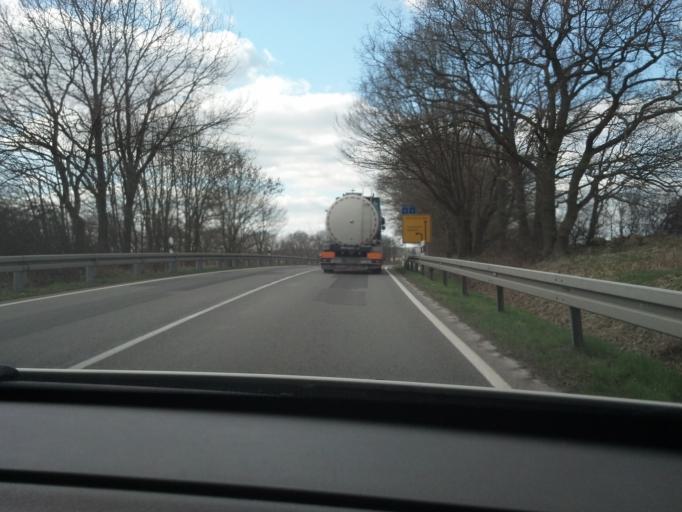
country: DE
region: Mecklenburg-Vorpommern
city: Malchow
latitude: 53.3685
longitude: 12.3677
